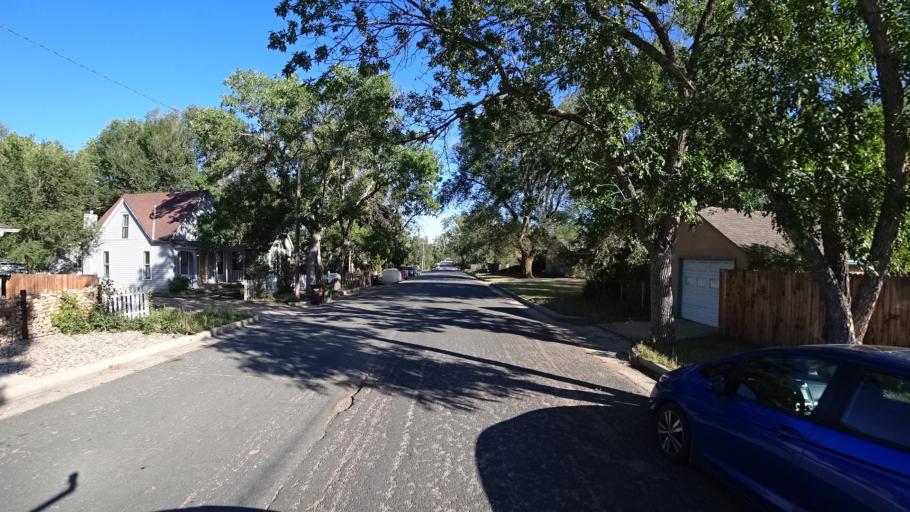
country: US
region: Colorado
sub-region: El Paso County
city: Colorado Springs
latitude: 38.8441
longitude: -104.8673
